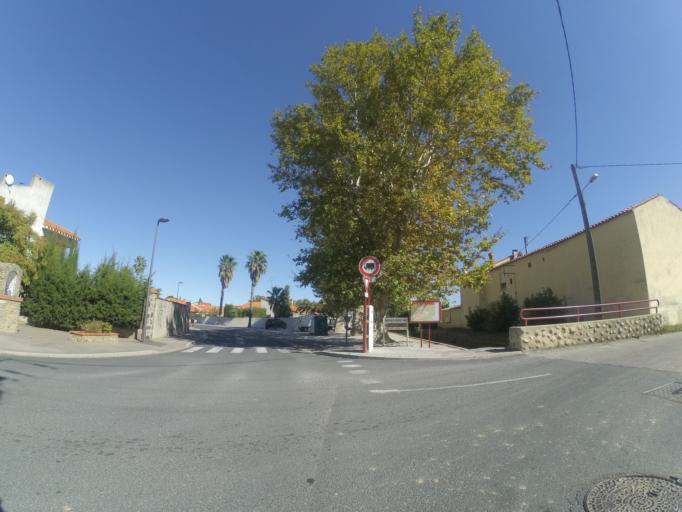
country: FR
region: Languedoc-Roussillon
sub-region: Departement des Pyrenees-Orientales
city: Baho
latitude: 42.6976
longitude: 2.8228
